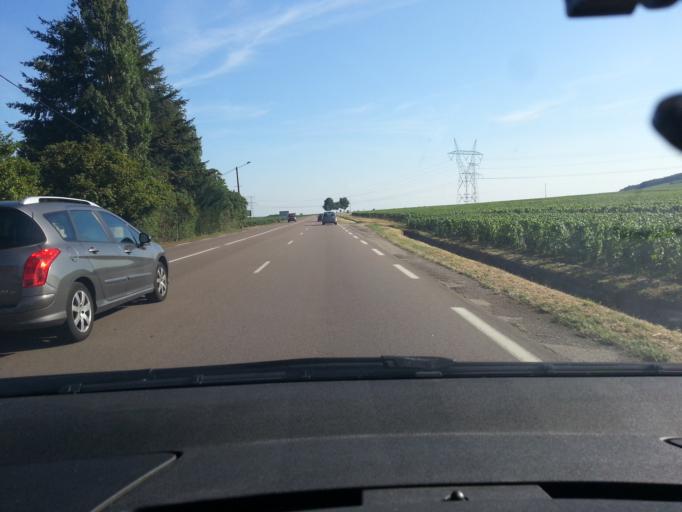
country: FR
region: Bourgogne
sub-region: Departement de la Cote-d'Or
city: Nuits-Saint-Georges
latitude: 47.1277
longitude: 4.9454
